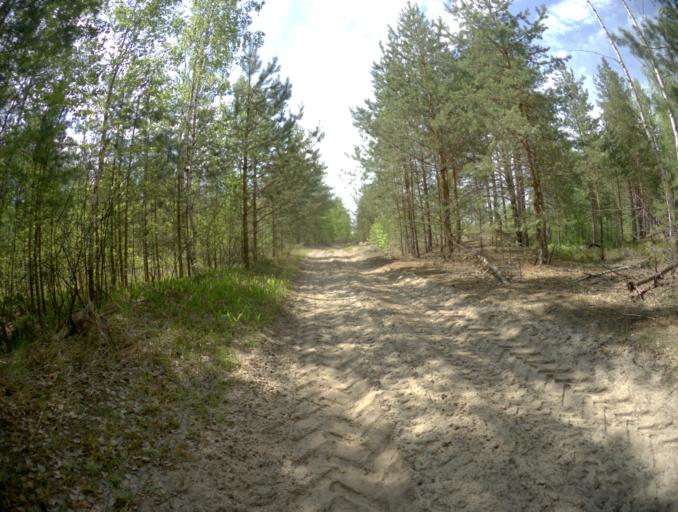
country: RU
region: Vladimir
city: Ivanishchi
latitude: 55.7039
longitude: 40.4520
